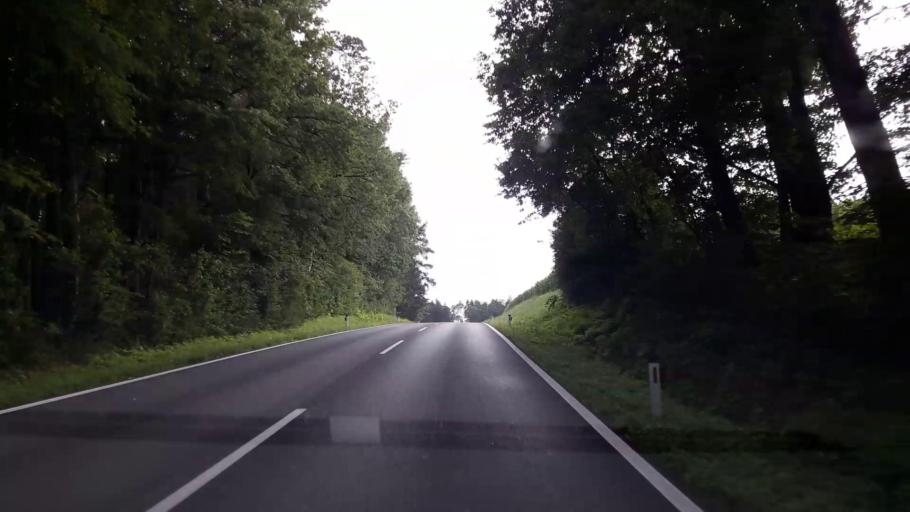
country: AT
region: Styria
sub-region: Politischer Bezirk Hartberg-Fuerstenfeld
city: Hartberg
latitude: 47.2590
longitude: 15.9394
